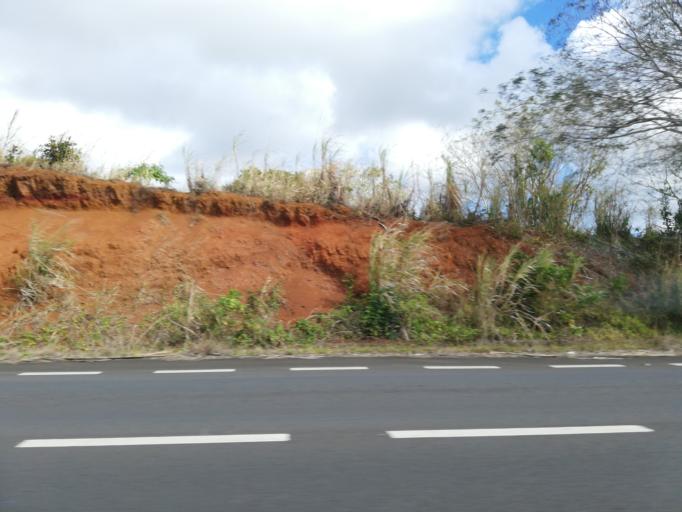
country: MU
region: Grand Port
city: Mahebourg
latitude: -20.4024
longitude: 57.6834
